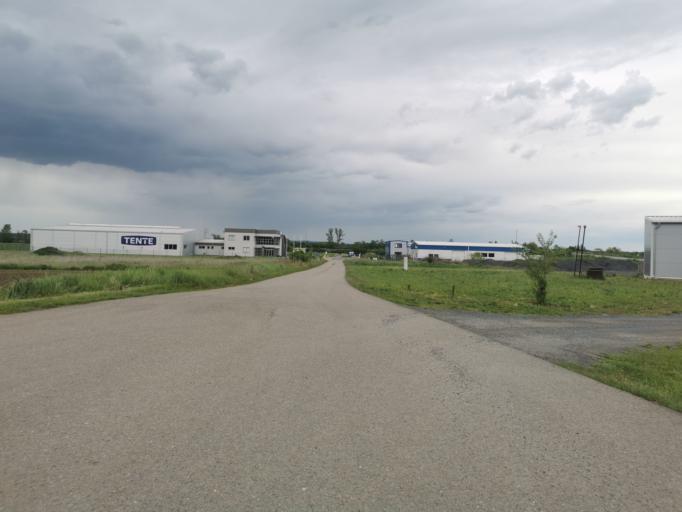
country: CZ
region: South Moravian
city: Sudomerice
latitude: 48.8719
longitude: 17.2394
